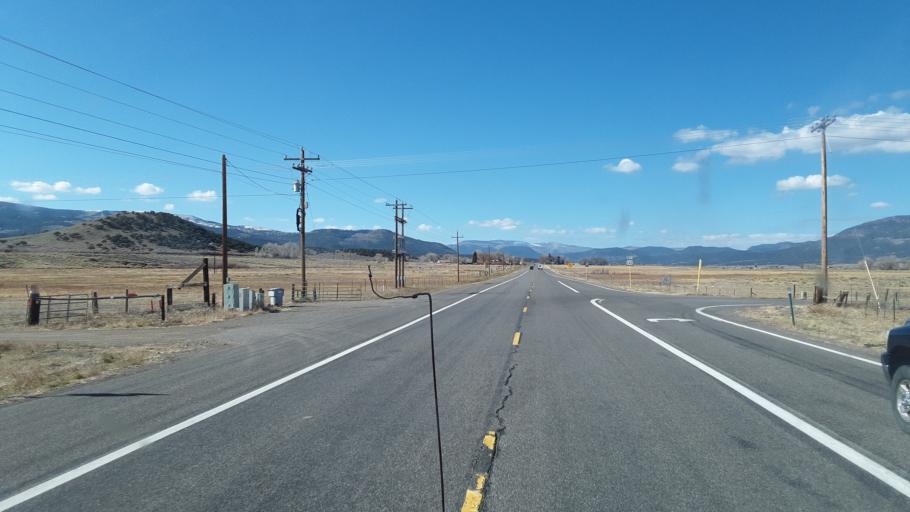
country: US
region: Colorado
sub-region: Rio Grande County
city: Del Norte
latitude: 37.6769
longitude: -106.4599
